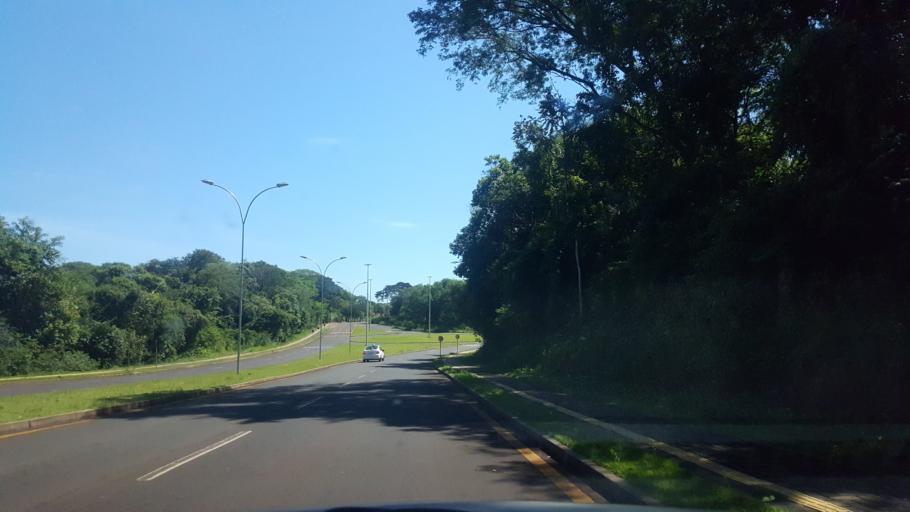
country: AR
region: Misiones
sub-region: Departamento de Iguazu
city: Puerto Iguazu
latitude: -25.5704
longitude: -54.5598
